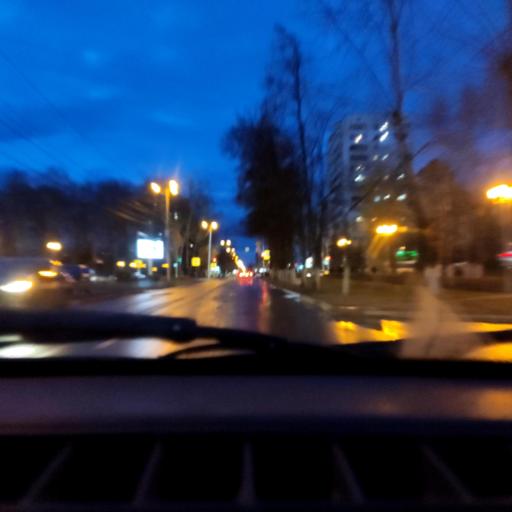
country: RU
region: Bashkortostan
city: Avdon
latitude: 54.7017
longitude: 55.8307
